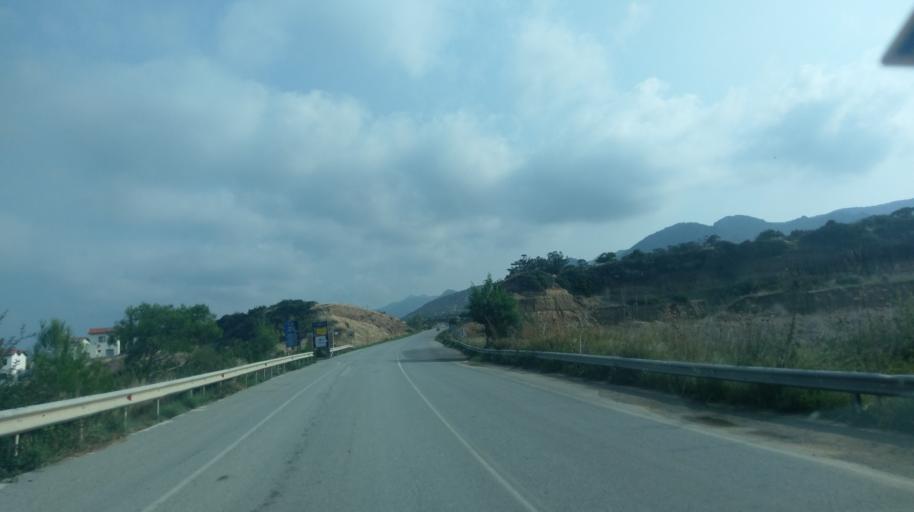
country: CY
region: Ammochostos
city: Lefkonoiko
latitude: 35.3539
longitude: 33.6346
